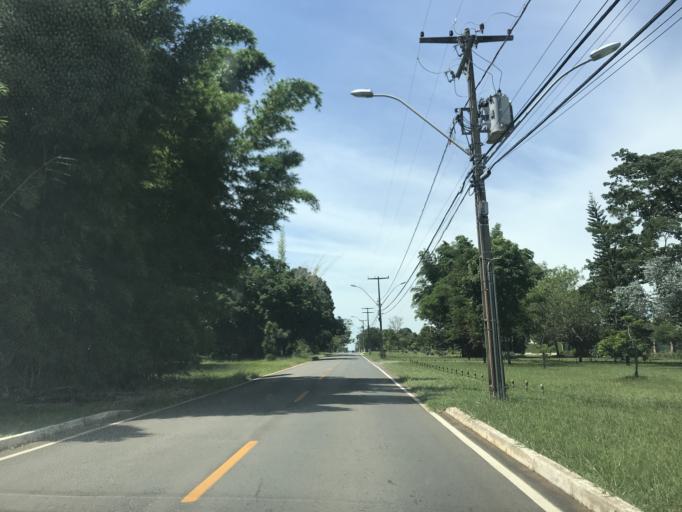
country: BR
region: Federal District
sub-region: Brasilia
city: Brasilia
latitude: -15.8994
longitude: -47.9325
